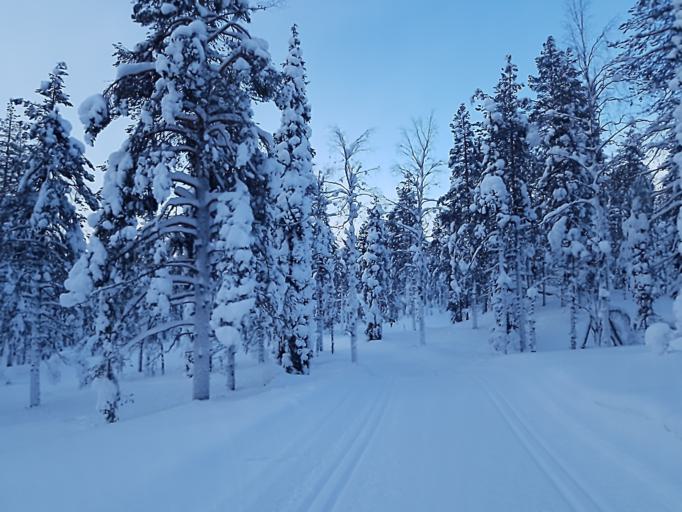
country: FI
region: Lapland
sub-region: Tunturi-Lappi
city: Kolari
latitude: 67.6476
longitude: 24.2380
